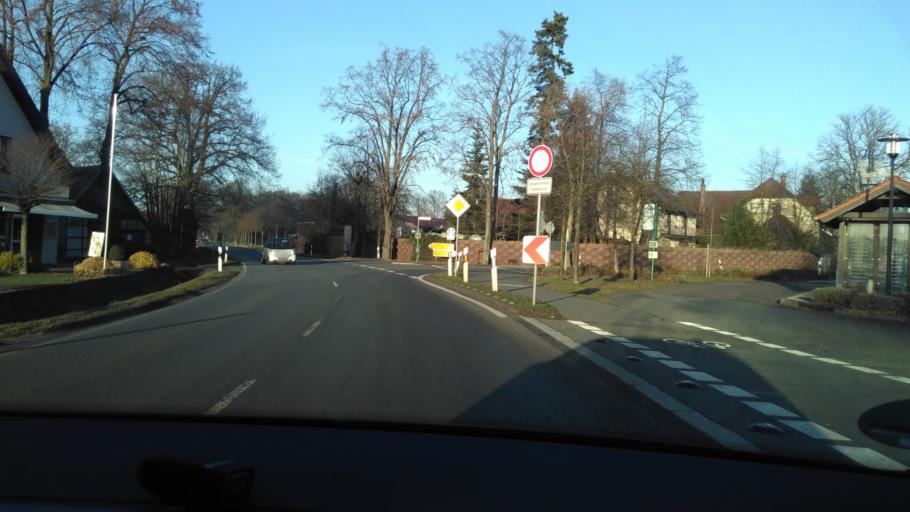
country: DE
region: North Rhine-Westphalia
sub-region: Regierungsbezirk Detmold
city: Verl
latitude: 51.9046
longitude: 8.5511
